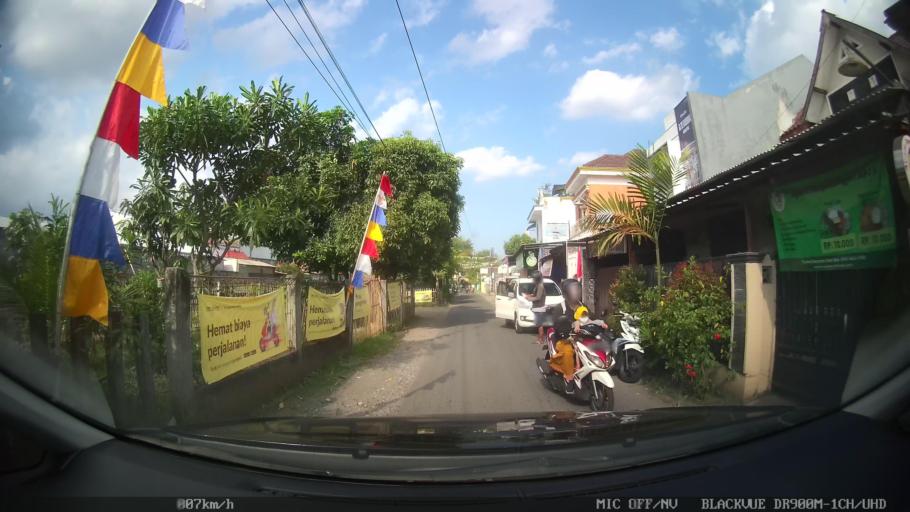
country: ID
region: Daerah Istimewa Yogyakarta
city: Yogyakarta
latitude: -7.7883
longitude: 110.3487
